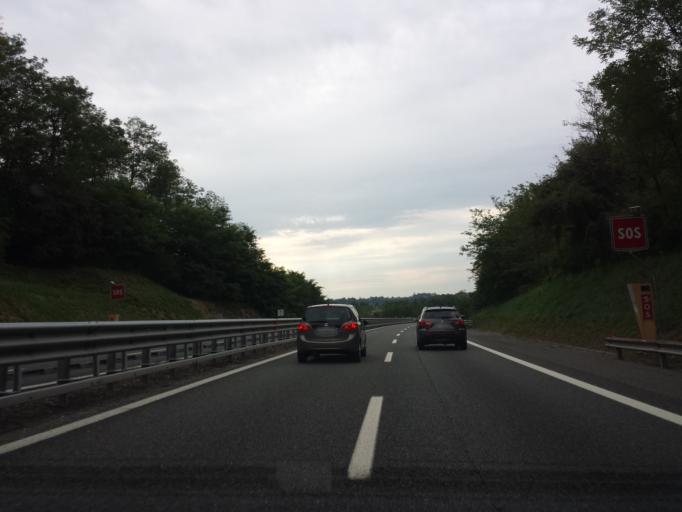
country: IT
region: Lombardy
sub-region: Provincia di Varese
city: Cavaria Con Premezzo
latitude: 45.6854
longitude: 8.7876
